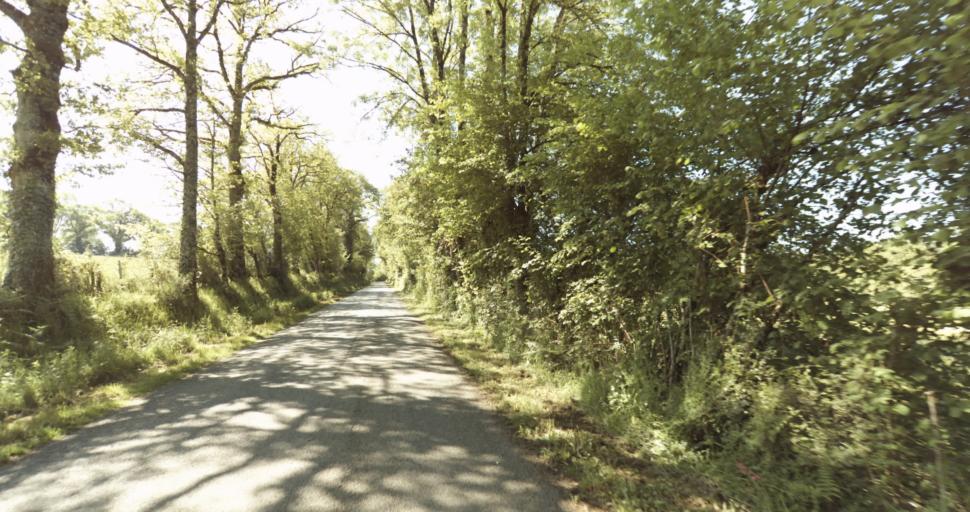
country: FR
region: Limousin
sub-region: Departement de la Haute-Vienne
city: Le Vigen
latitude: 45.7263
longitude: 1.2864
